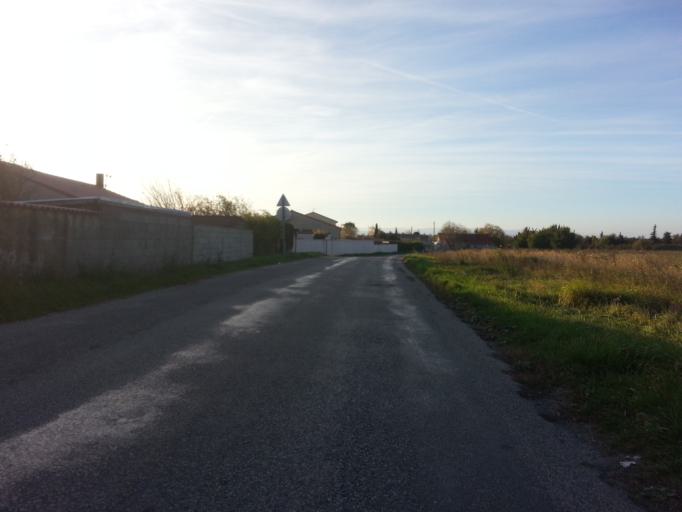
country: FR
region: Rhone-Alpes
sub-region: Departement de la Drome
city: Chabeuil
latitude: 44.9049
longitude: 5.0159
